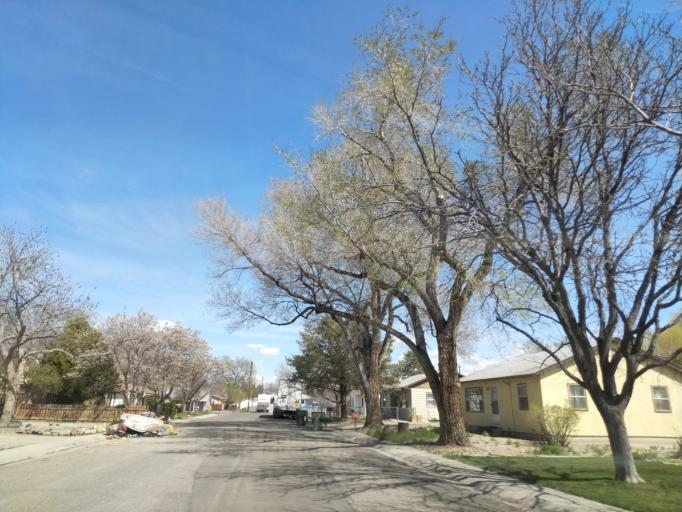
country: US
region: Colorado
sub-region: Mesa County
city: Grand Junction
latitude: 39.0801
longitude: -108.5275
